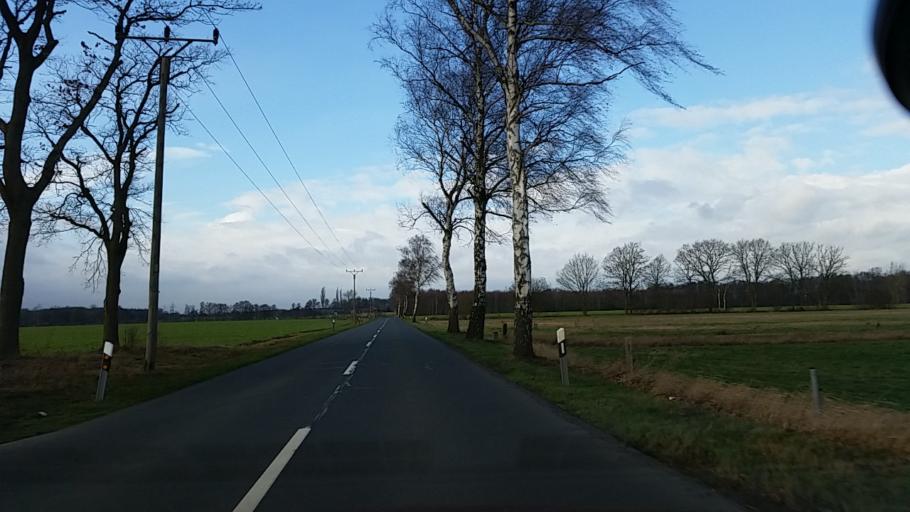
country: DE
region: Lower Saxony
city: Wrestedt
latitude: 52.9078
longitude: 10.5551
